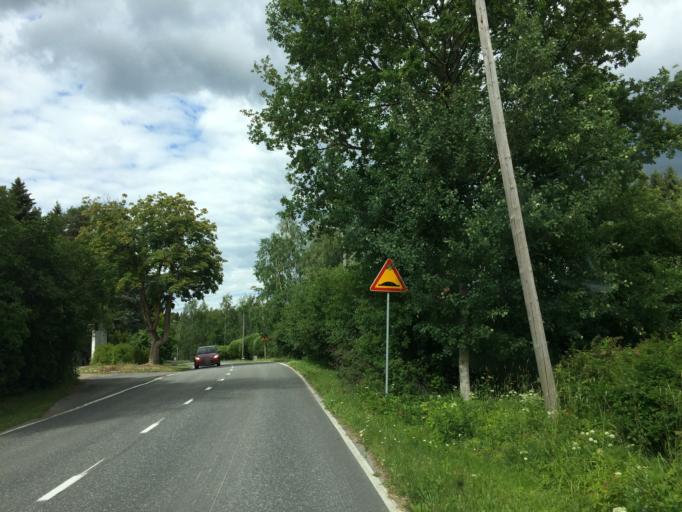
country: FI
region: Haeme
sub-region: Haemeenlinna
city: Tervakoski
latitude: 60.8242
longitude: 24.6218
